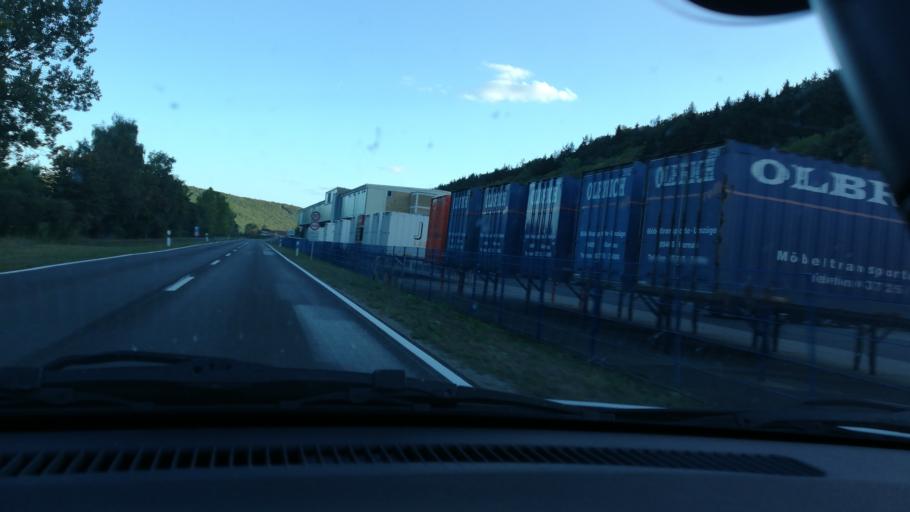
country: DE
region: Bavaria
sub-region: Regierungsbezirk Unterfranken
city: Hafenlohr
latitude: 49.8802
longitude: 9.5998
